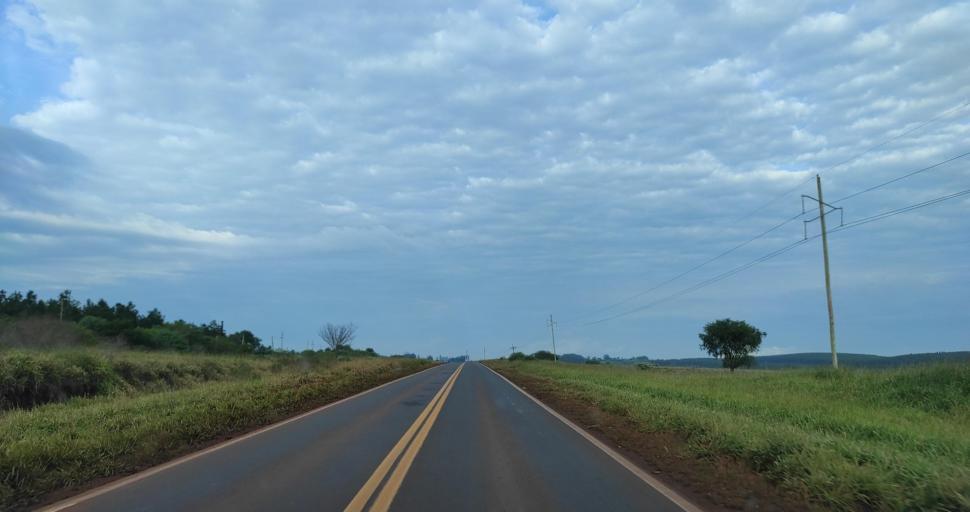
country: AR
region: Corrientes
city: Gobernador Ingeniero Valentin Virasoro
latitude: -27.9230
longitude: -55.9611
